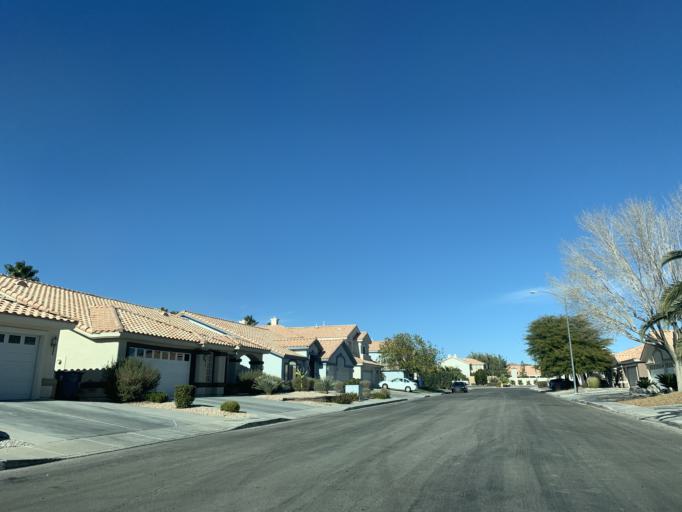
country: US
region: Nevada
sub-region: Clark County
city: Summerlin South
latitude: 36.1169
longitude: -115.2943
